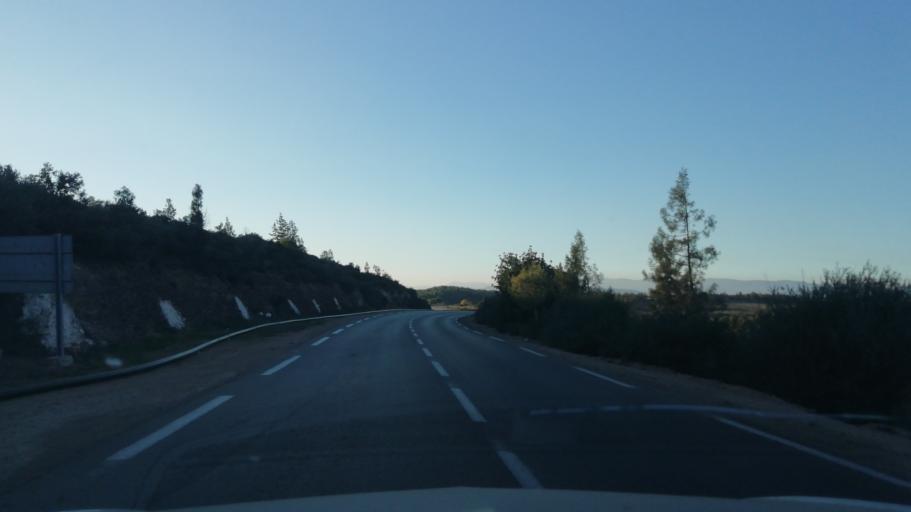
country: DZ
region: Tlemcen
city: Beni Mester
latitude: 34.8126
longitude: -1.6249
